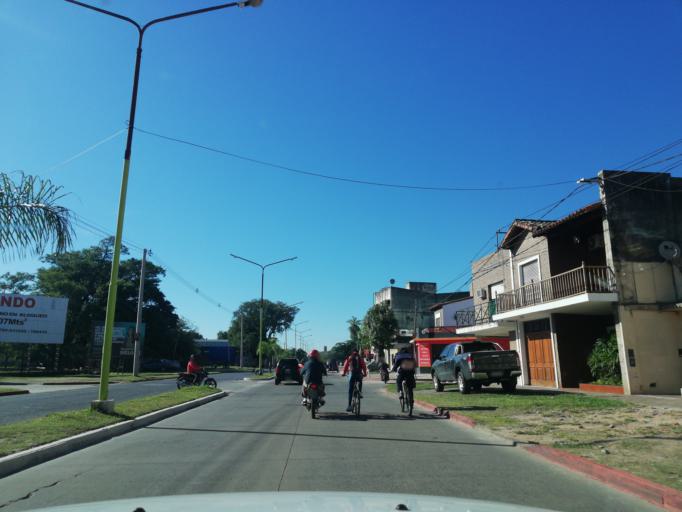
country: AR
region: Corrientes
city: Corrientes
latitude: -27.4734
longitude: -58.8037
